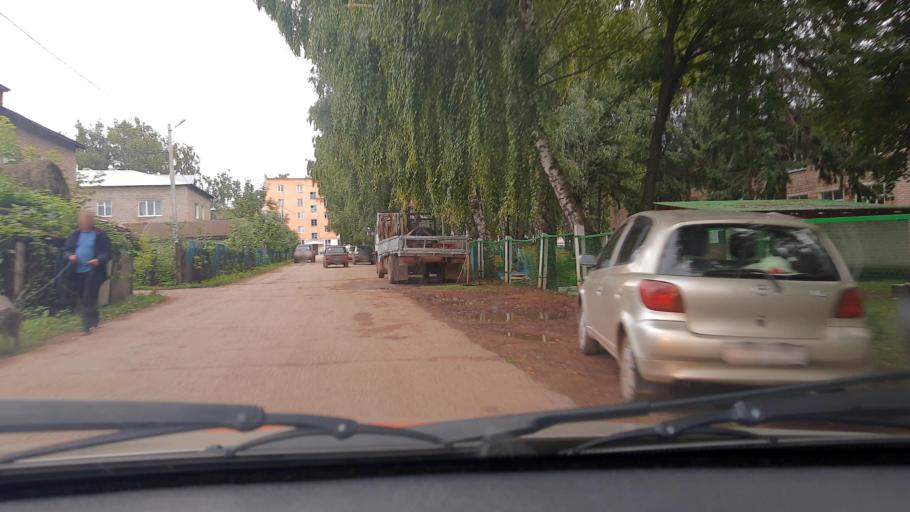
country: RU
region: Bashkortostan
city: Chishmy
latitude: 54.5903
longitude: 55.3760
